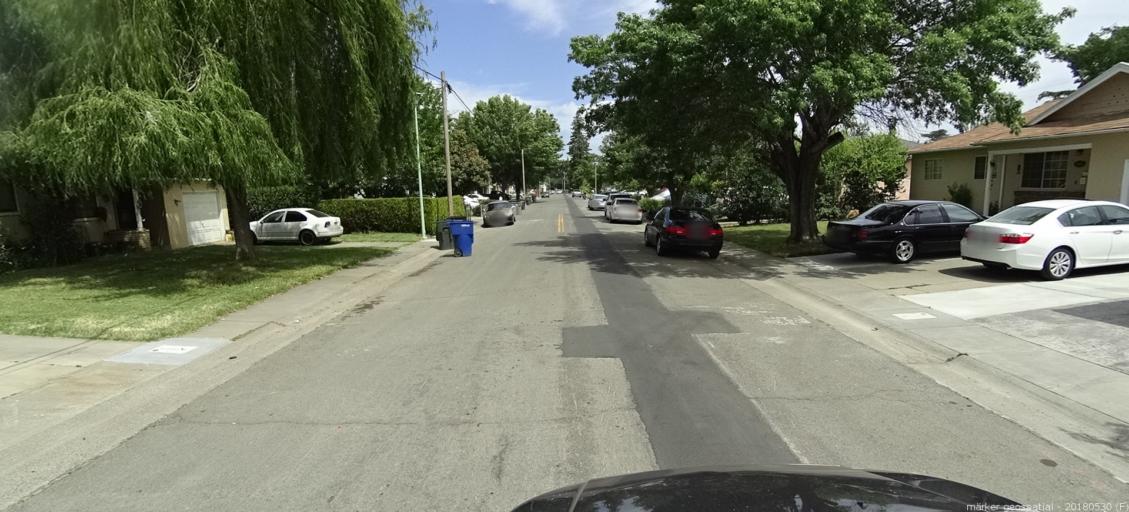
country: US
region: California
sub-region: Sacramento County
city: Sacramento
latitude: 38.6134
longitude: -121.4826
